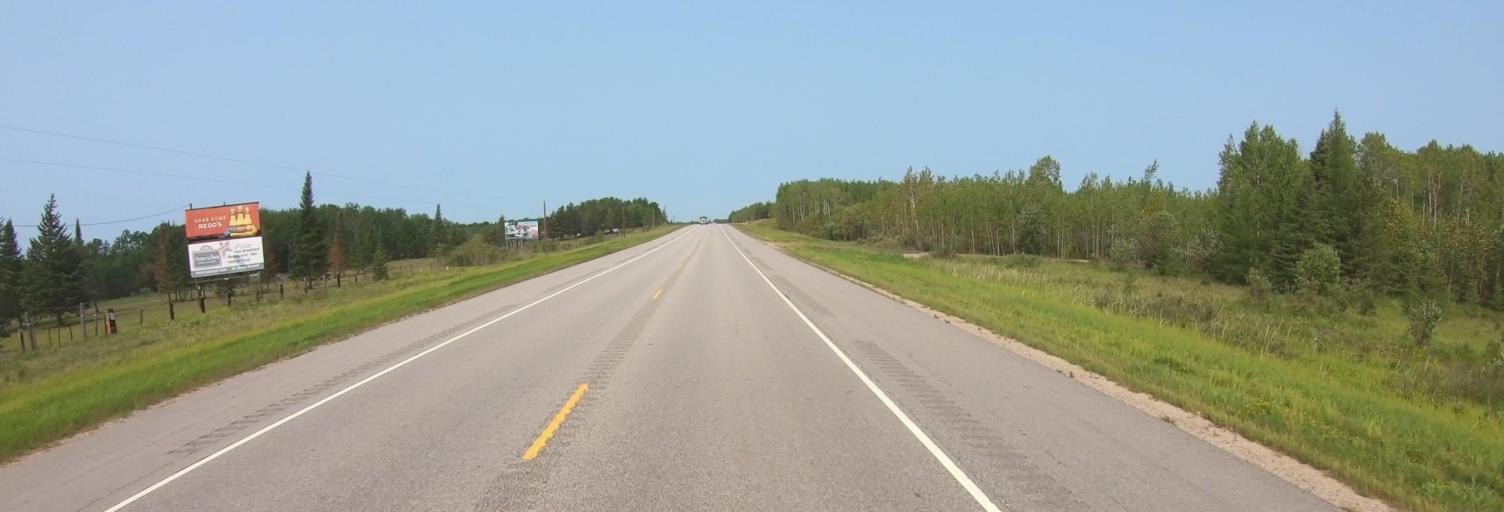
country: CA
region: Ontario
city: Fort Frances
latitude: 48.4154
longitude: -93.2106
